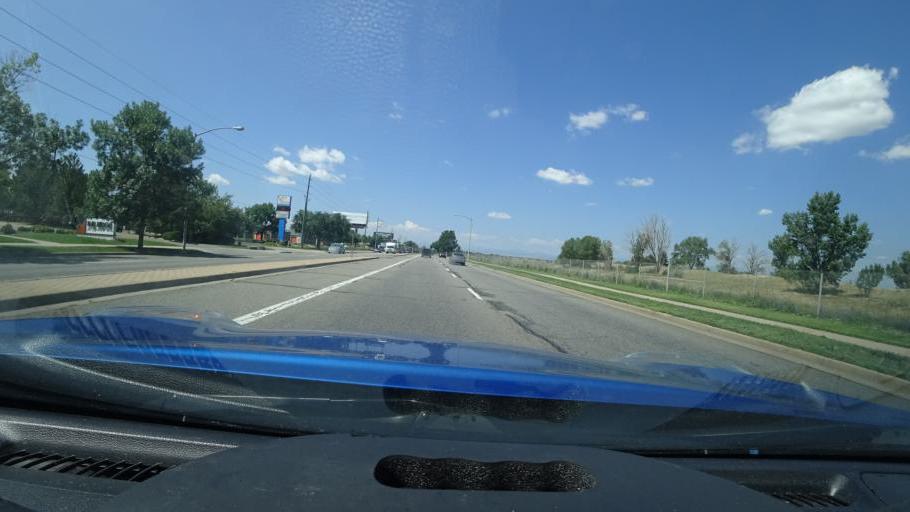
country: US
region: Colorado
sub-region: Adams County
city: Aurora
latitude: 39.7099
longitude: -104.8718
